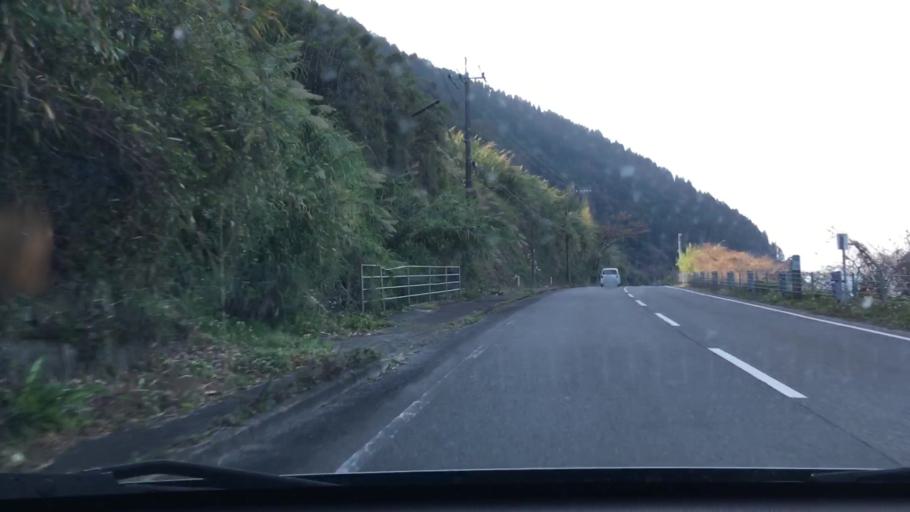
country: JP
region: Kagoshima
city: Kokubu-matsuki
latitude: 31.6368
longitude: 130.8061
